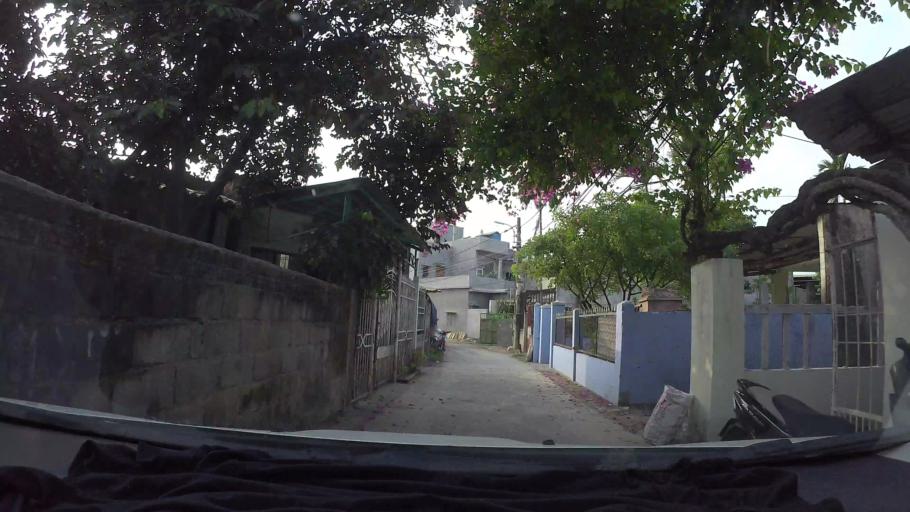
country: VN
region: Da Nang
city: Lien Chieu
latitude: 16.0492
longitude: 108.1517
